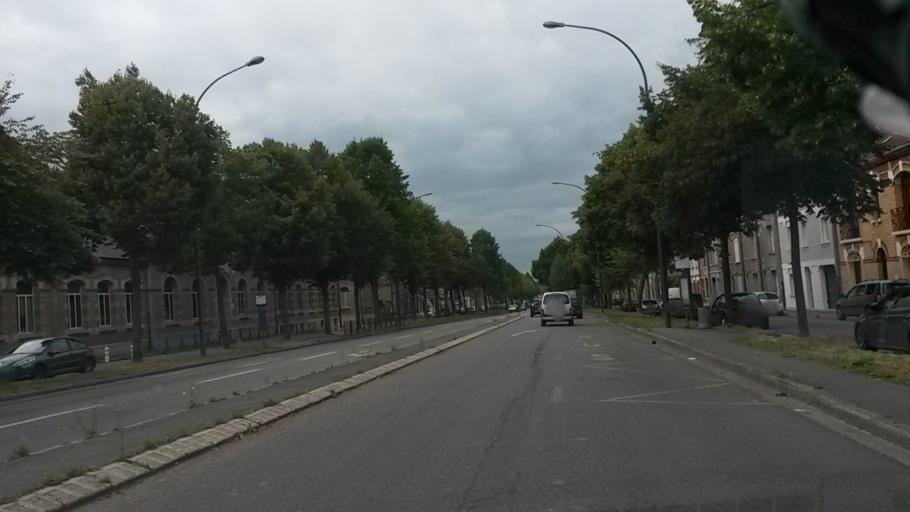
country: FR
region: Picardie
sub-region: Departement de la Somme
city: Amiens
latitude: 49.8840
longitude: 2.2821
